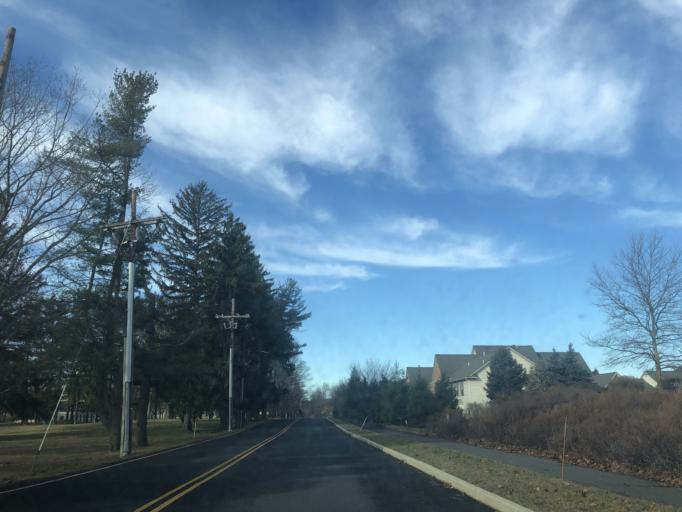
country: US
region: New Jersey
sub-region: Somerset County
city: Kingston
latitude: 40.3591
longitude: -74.6173
